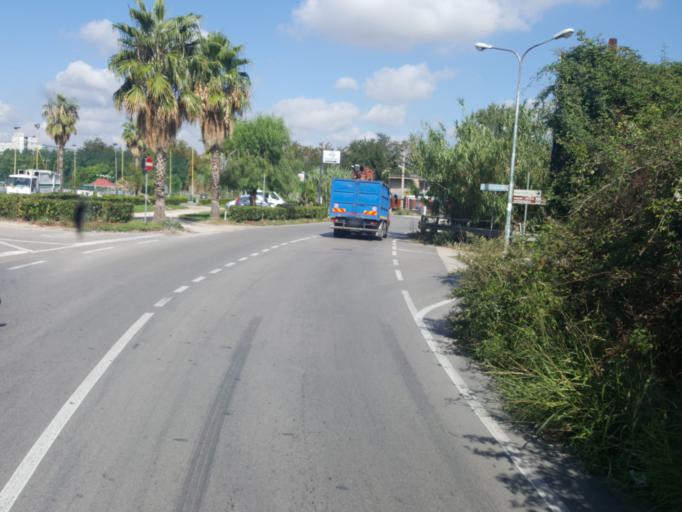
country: IT
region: Campania
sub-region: Provincia di Napoli
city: Nola
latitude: 40.9307
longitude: 14.5106
